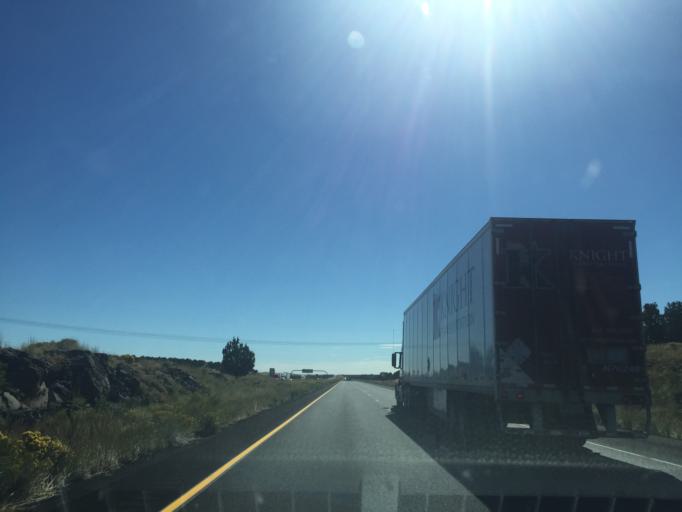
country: US
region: Arizona
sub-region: Coconino County
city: Flagstaff
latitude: 35.1977
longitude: -111.3975
